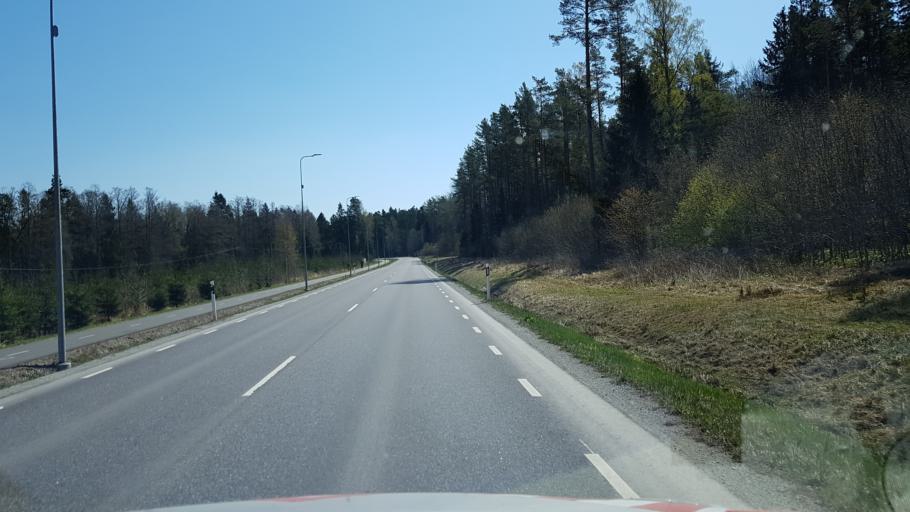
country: EE
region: Harju
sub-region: Viimsi vald
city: Viimsi
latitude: 59.5260
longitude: 24.8828
